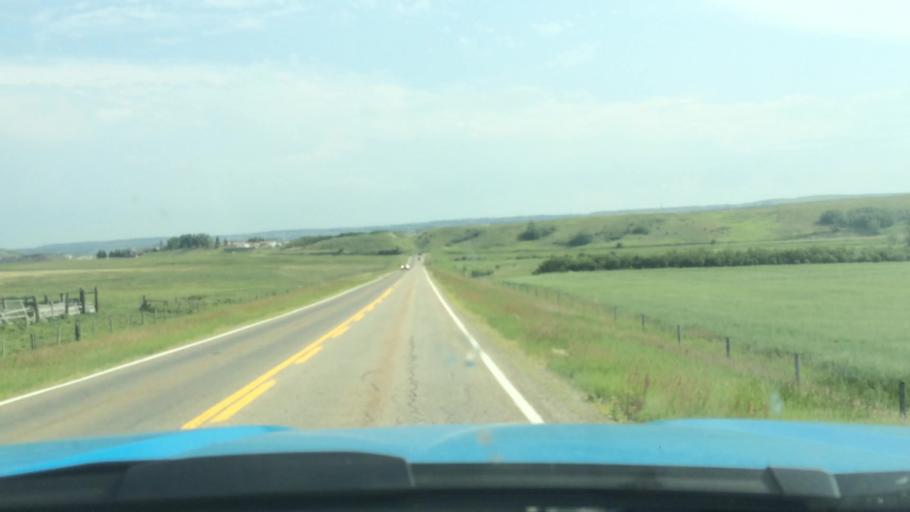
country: CA
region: Alberta
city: Airdrie
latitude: 51.1931
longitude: -114.1404
